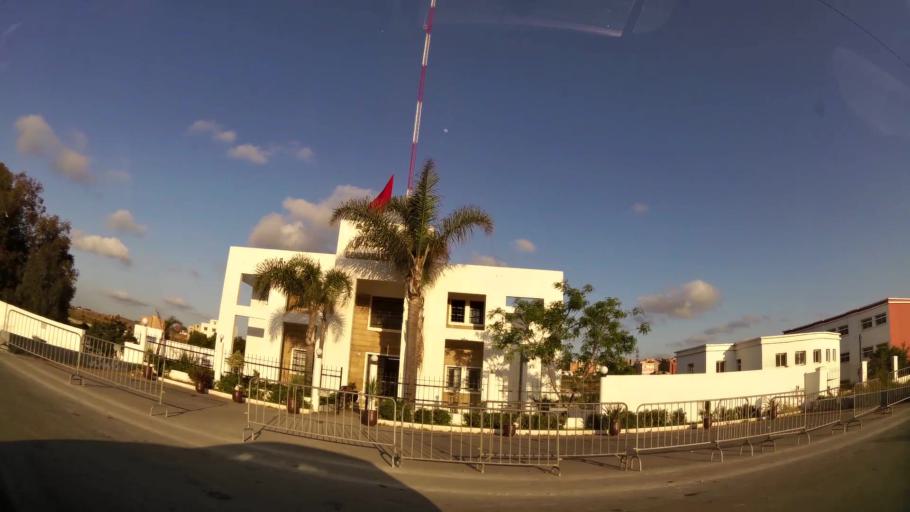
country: MA
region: Rabat-Sale-Zemmour-Zaer
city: Sale
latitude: 34.1280
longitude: -6.7351
